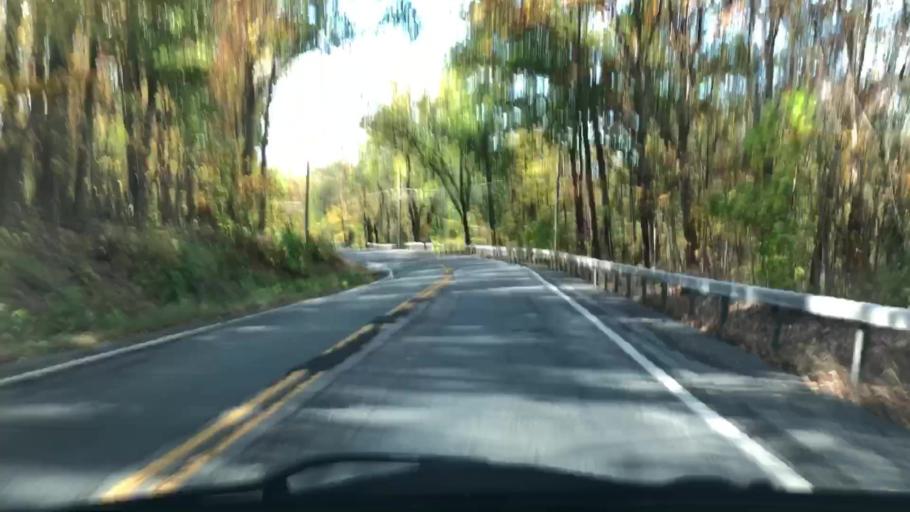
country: US
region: New York
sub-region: Orange County
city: Walden
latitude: 41.5814
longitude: -74.1874
